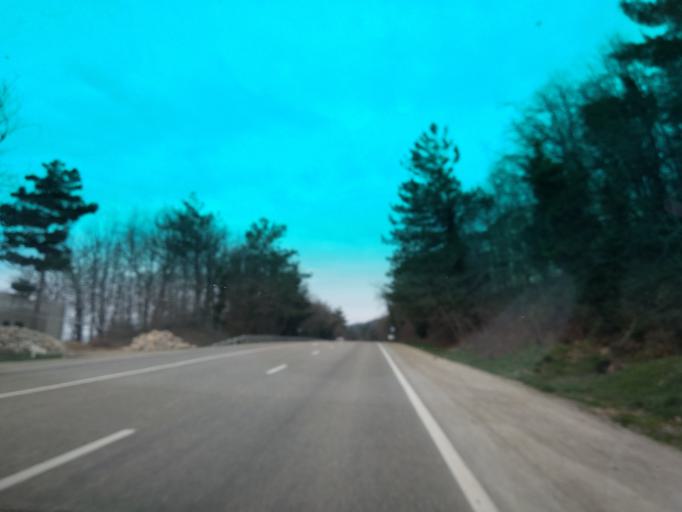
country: RU
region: Krasnodarskiy
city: Ol'ginka
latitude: 44.1802
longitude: 38.9374
